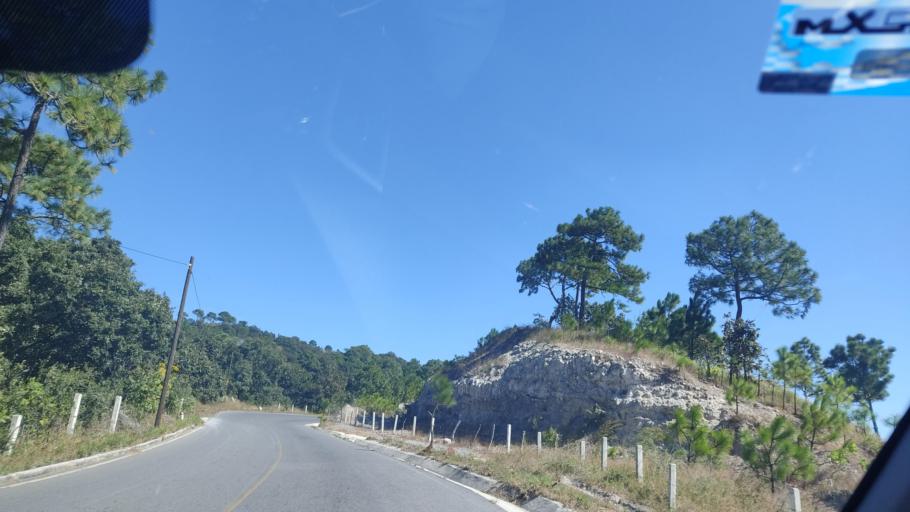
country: MX
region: Nayarit
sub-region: Jala
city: Rosa Blanca
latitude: 21.1011
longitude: -104.3712
